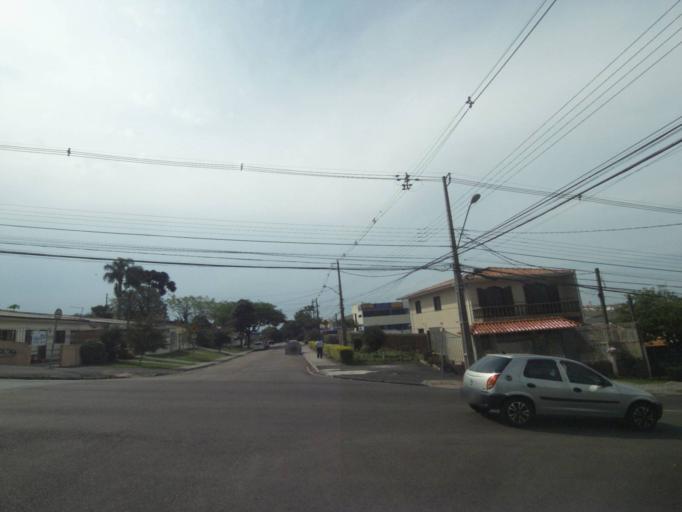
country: BR
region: Parana
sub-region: Pinhais
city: Pinhais
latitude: -25.4078
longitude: -49.2098
